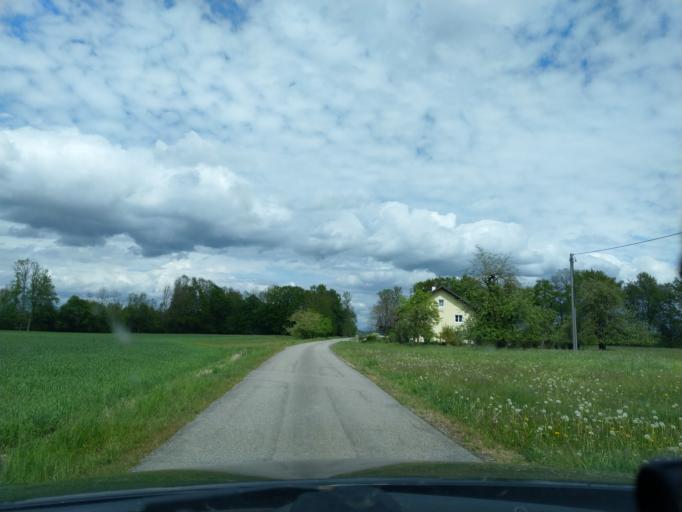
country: DE
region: Bavaria
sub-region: Lower Bavaria
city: Bad Fussing
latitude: 48.2770
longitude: 13.3169
